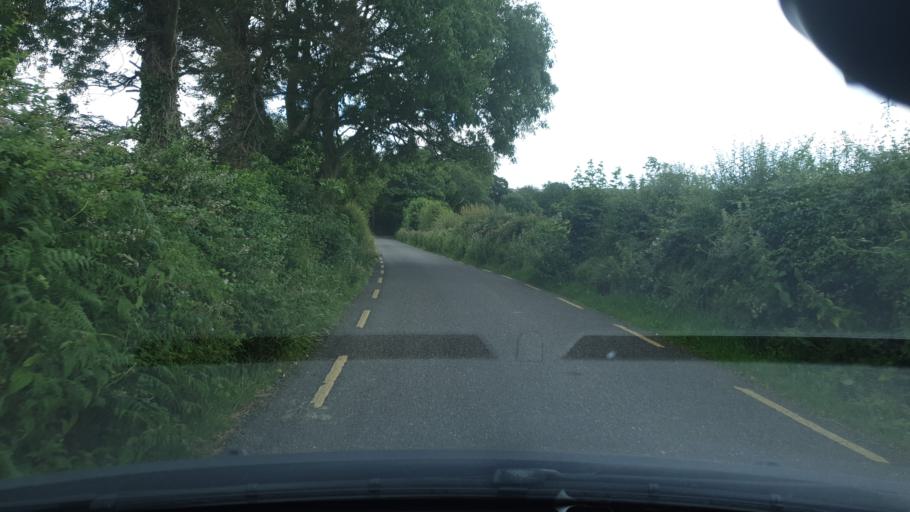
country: IE
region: Munster
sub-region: Ciarrai
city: Tralee
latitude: 52.2482
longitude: -9.6451
